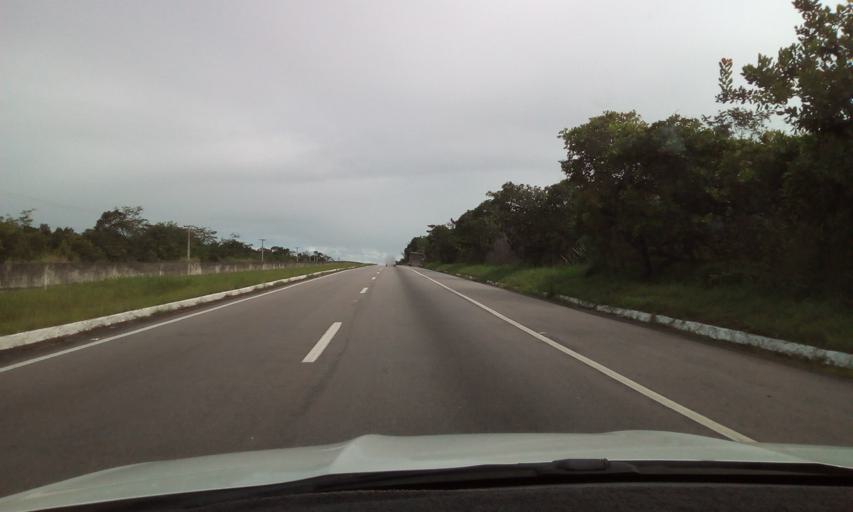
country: BR
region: Paraiba
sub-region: Alhandra
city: Alhandra
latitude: -7.4178
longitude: -34.9599
